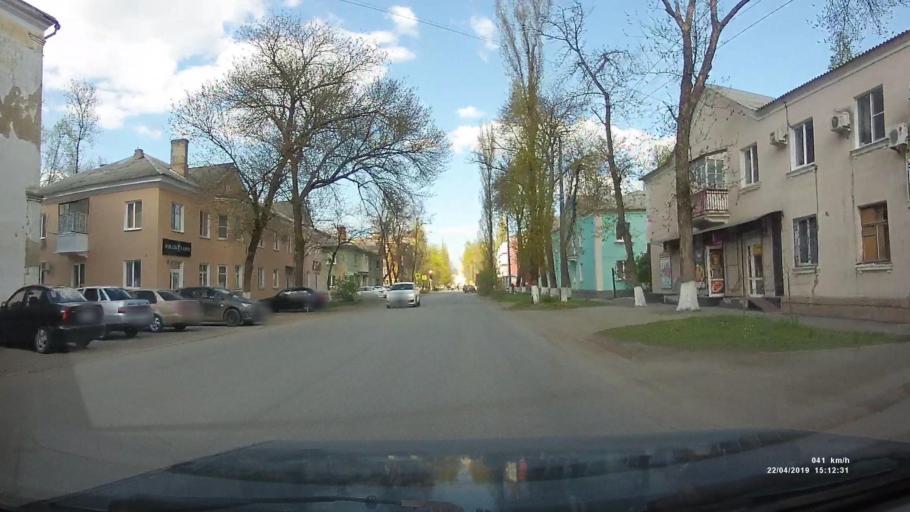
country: RU
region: Rostov
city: Azov
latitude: 47.1008
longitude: 39.4206
